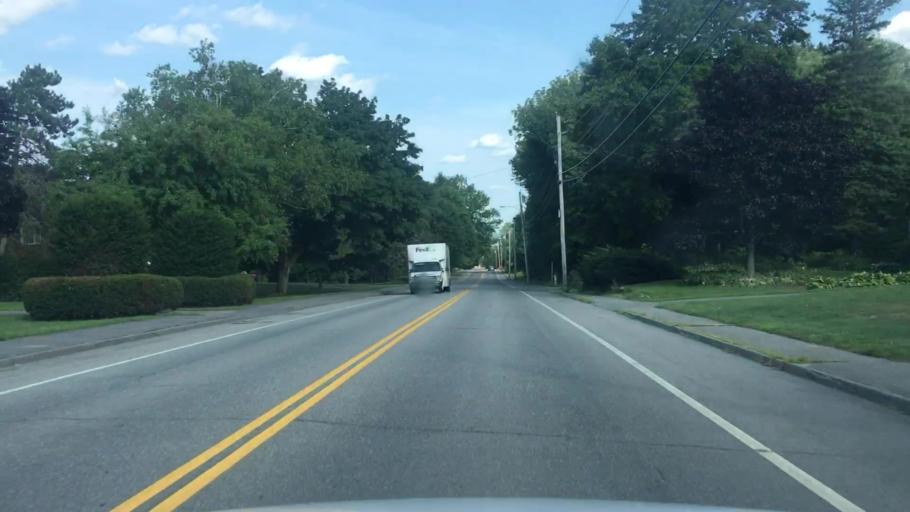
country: US
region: Maine
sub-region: Kennebec County
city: Waterville
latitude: 44.5562
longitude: -69.6540
